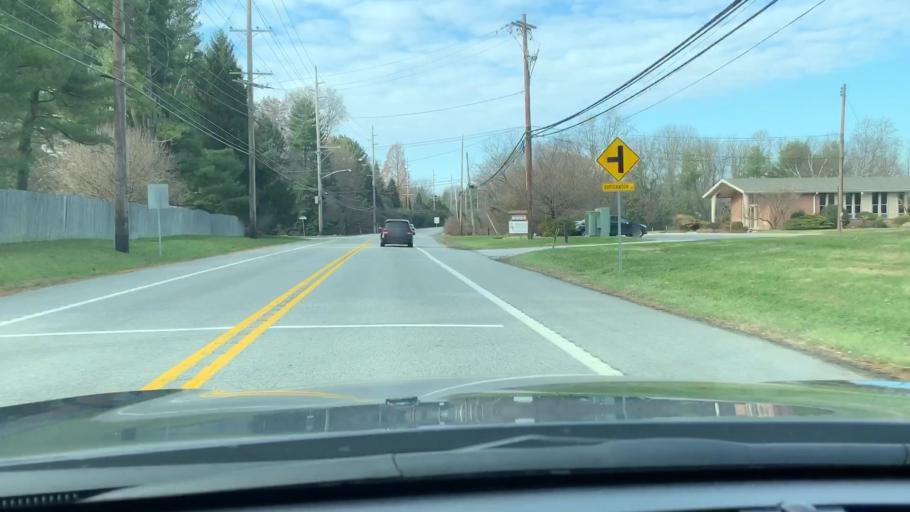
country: US
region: Pennsylvania
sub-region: Chester County
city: Berwyn
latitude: 40.0165
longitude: -75.4398
